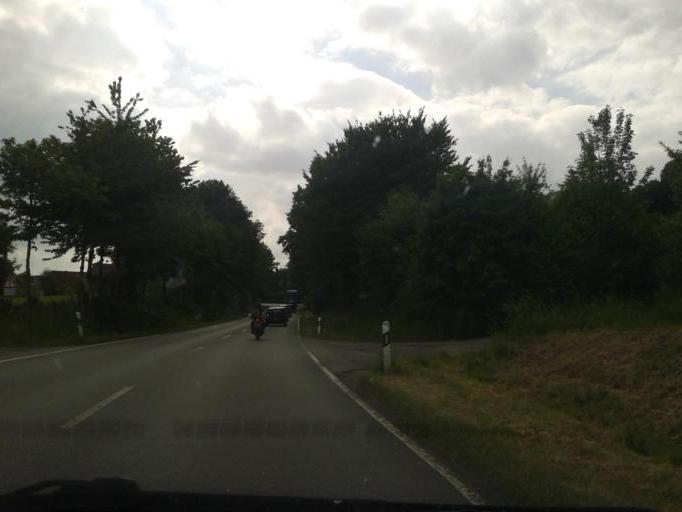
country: DE
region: North Rhine-Westphalia
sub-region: Regierungsbezirk Detmold
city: Steinheim
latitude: 51.8998
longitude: 9.1058
